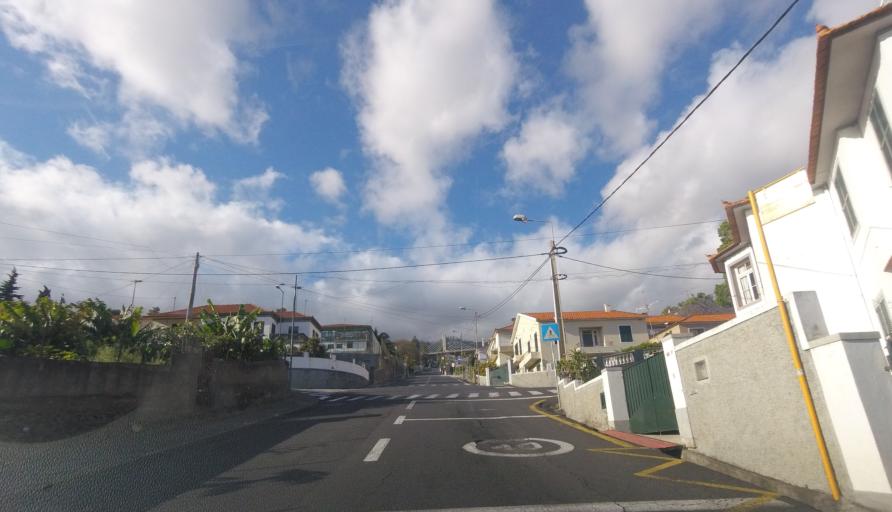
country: PT
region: Madeira
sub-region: Funchal
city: Nossa Senhora do Monte
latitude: 32.6583
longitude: -16.9090
